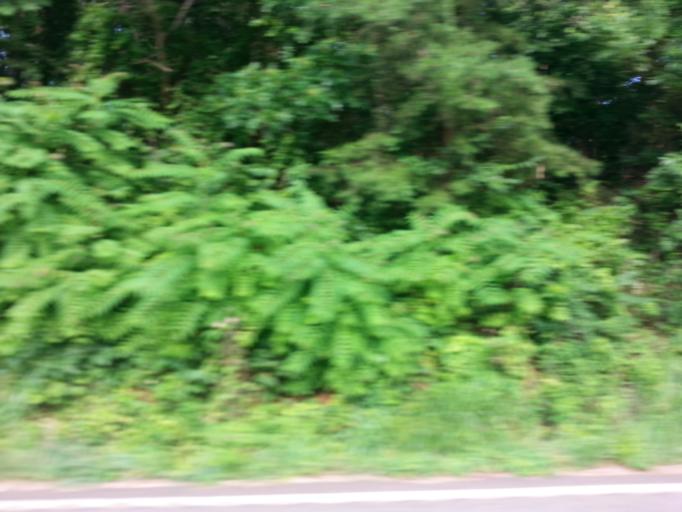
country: US
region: Tennessee
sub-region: Loudon County
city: Greenback
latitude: 35.6485
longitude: -84.1038
